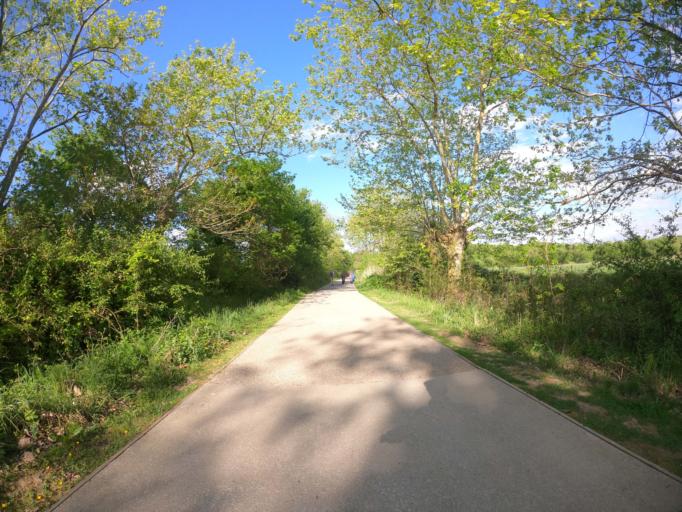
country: FR
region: Aquitaine
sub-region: Departement des Pyrenees-Atlantiques
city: Bayonne
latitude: 43.4751
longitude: -1.4772
